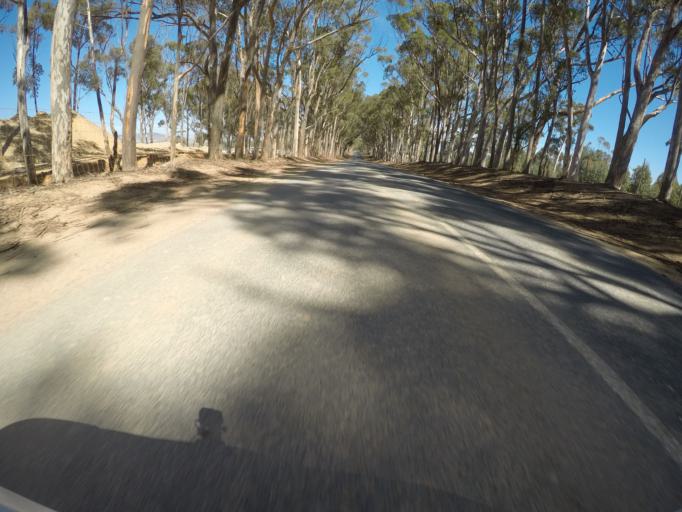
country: ZA
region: Western Cape
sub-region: City of Cape Town
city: Sunset Beach
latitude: -33.7603
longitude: 18.5532
